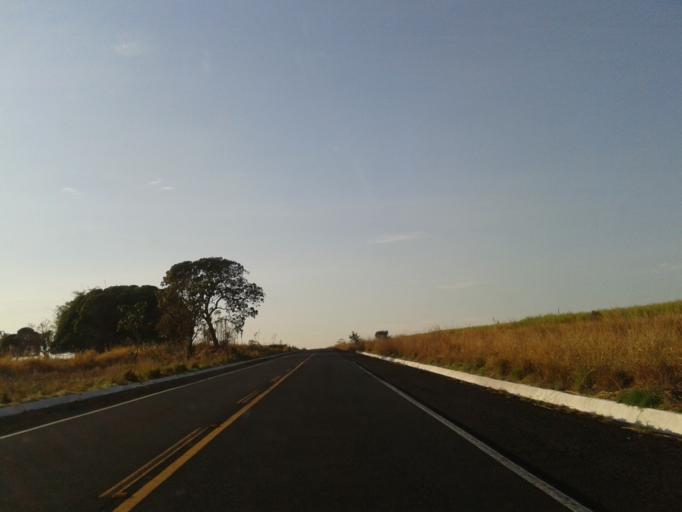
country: BR
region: Minas Gerais
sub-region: Santa Vitoria
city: Santa Vitoria
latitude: -19.1162
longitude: -50.3105
